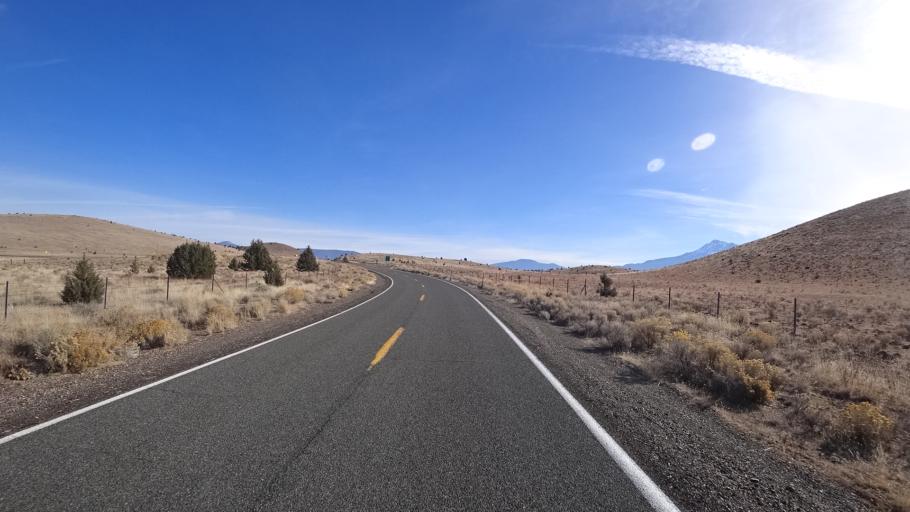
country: US
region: California
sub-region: Siskiyou County
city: Weed
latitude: 41.5512
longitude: -122.4886
